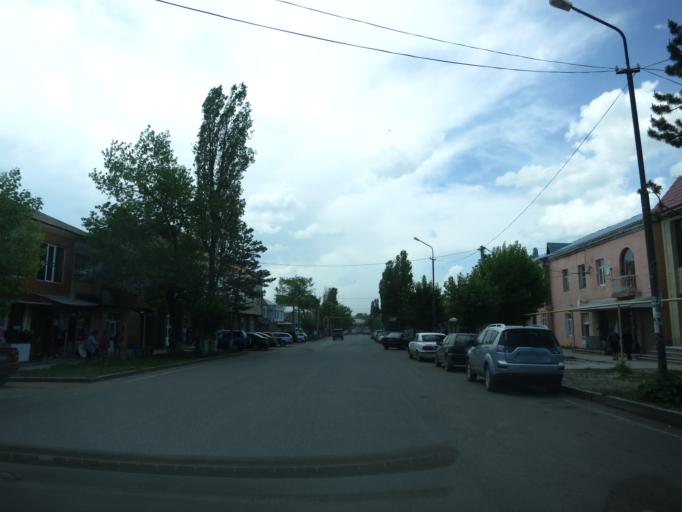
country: GE
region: Samtskhe-Javakheti
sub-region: Ninotsminda
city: Ninotsminda
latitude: 41.2664
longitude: 43.5912
